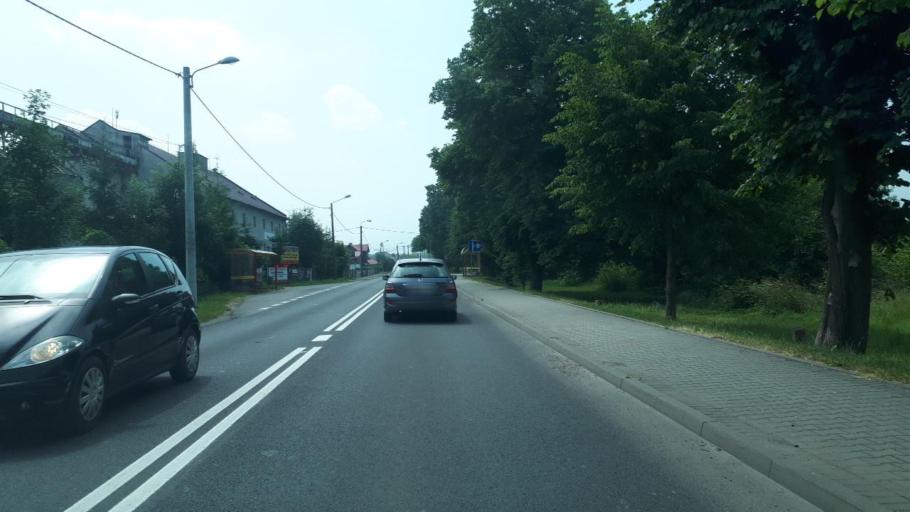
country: PL
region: Silesian Voivodeship
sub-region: Powiat cieszynski
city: Ustron
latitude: 49.7451
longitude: 18.8037
